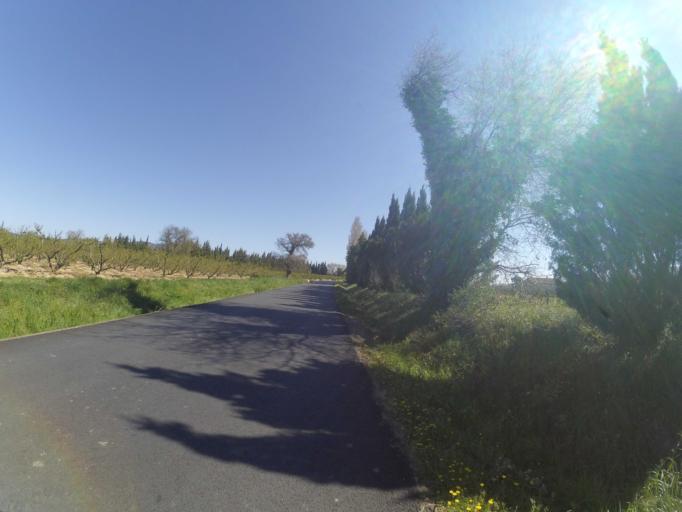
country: FR
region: Languedoc-Roussillon
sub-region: Departement des Pyrenees-Orientales
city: Millas
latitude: 42.6763
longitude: 2.6679
